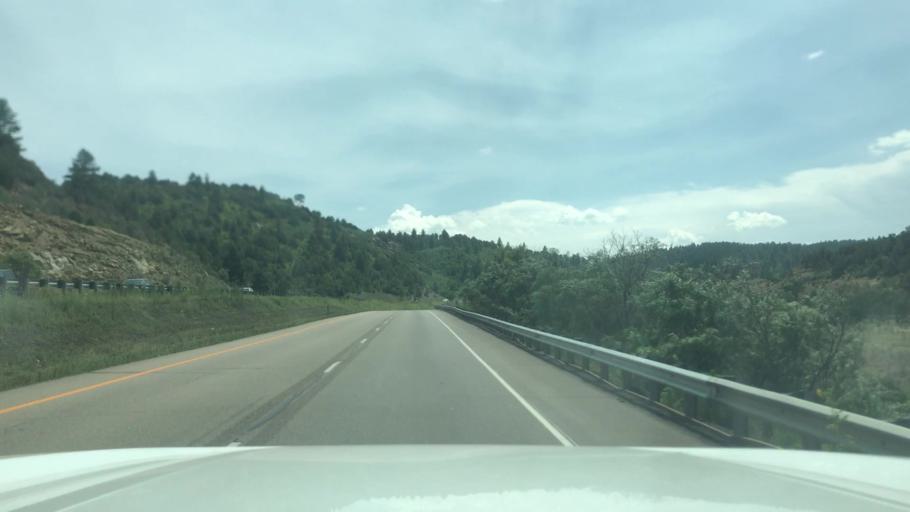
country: US
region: Colorado
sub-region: Las Animas County
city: Trinidad
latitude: 37.0683
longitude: -104.5184
